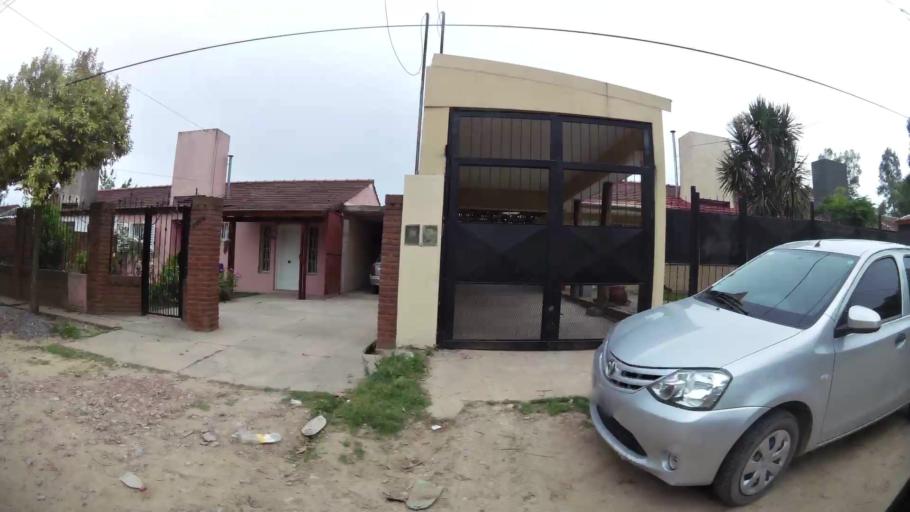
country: AR
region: Buenos Aires
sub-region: Partido de Campana
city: Campana
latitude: -34.2134
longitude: -58.9429
